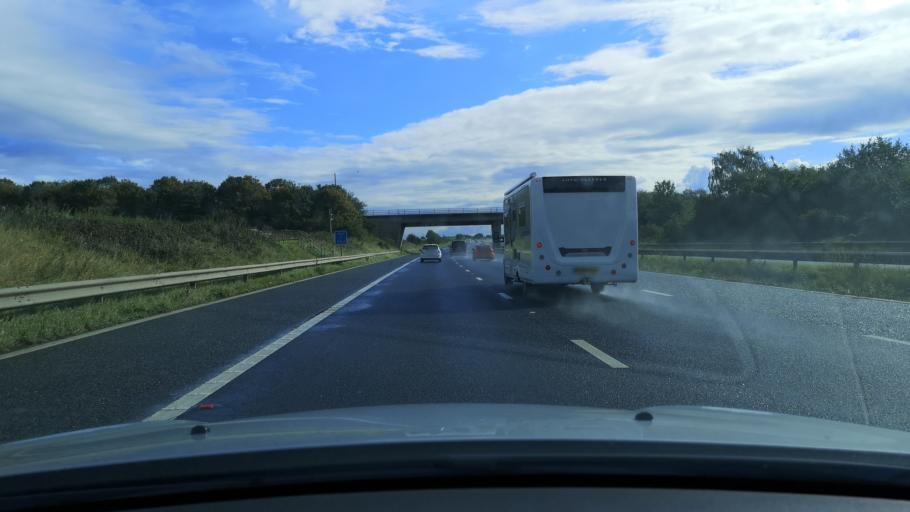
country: GB
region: England
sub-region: East Riding of Yorkshire
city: Pollington
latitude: 53.6939
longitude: -1.1217
